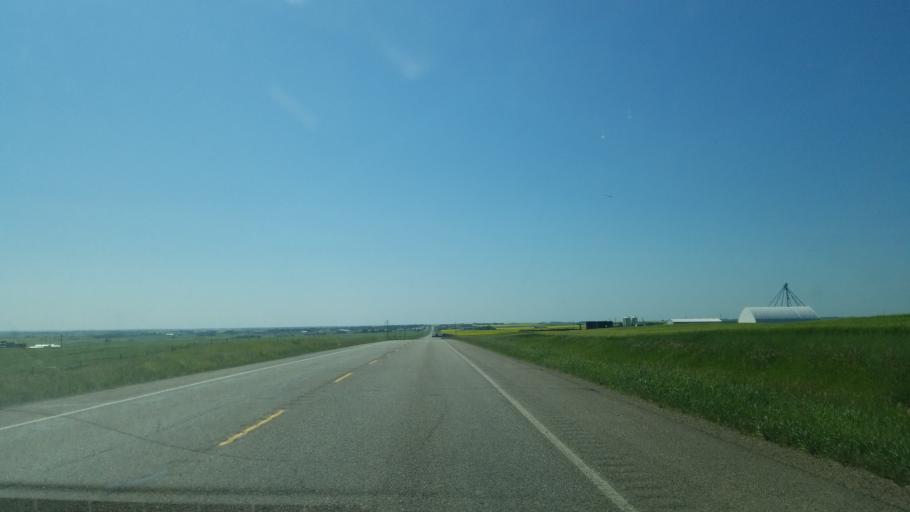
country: CA
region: Alberta
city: Provost
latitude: 52.3612
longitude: -110.1873
